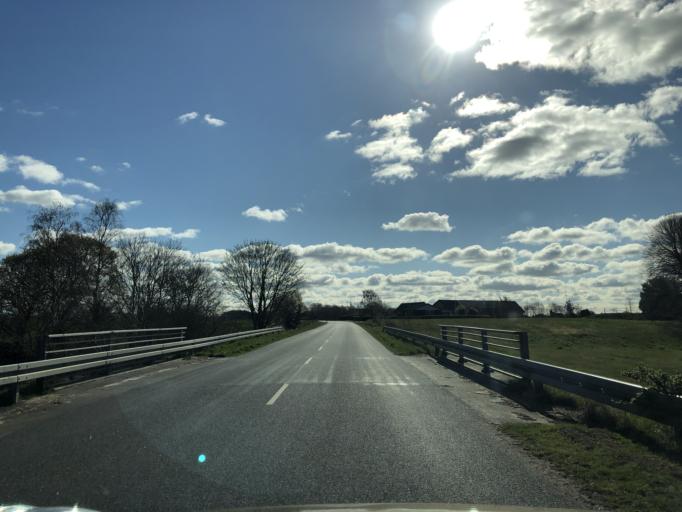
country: DK
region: North Denmark
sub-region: Vesthimmerland Kommune
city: Alestrup
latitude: 56.6066
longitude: 9.5539
